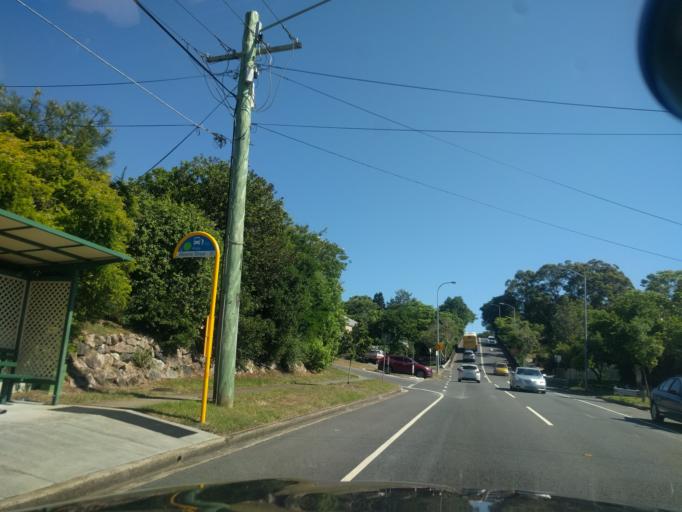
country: AU
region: Queensland
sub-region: Brisbane
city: Stafford
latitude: -27.4032
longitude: 153.0091
